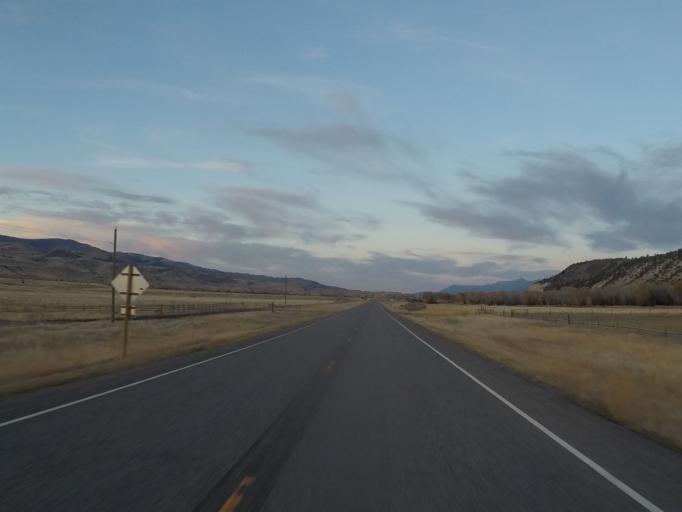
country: US
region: Montana
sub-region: Gallatin County
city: Bozeman
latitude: 45.2876
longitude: -110.8430
